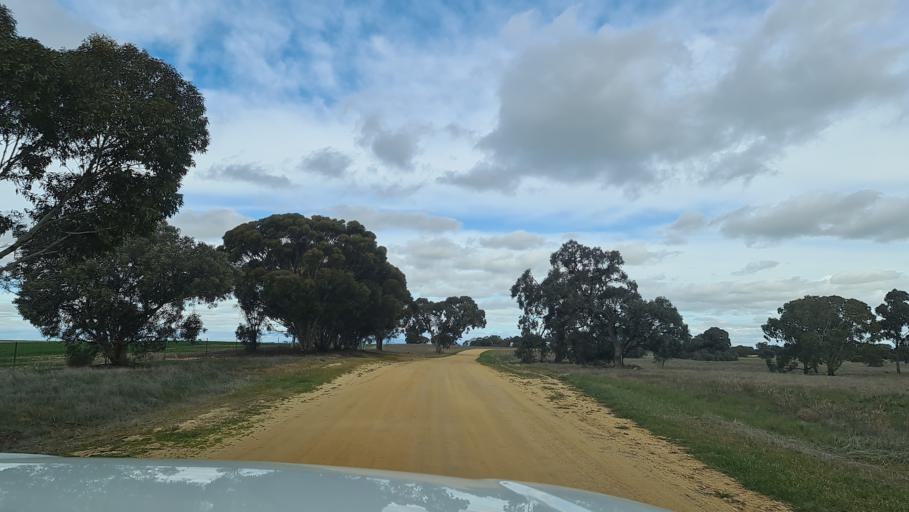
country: AU
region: Victoria
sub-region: Horsham
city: Horsham
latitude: -36.6160
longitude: 142.4232
